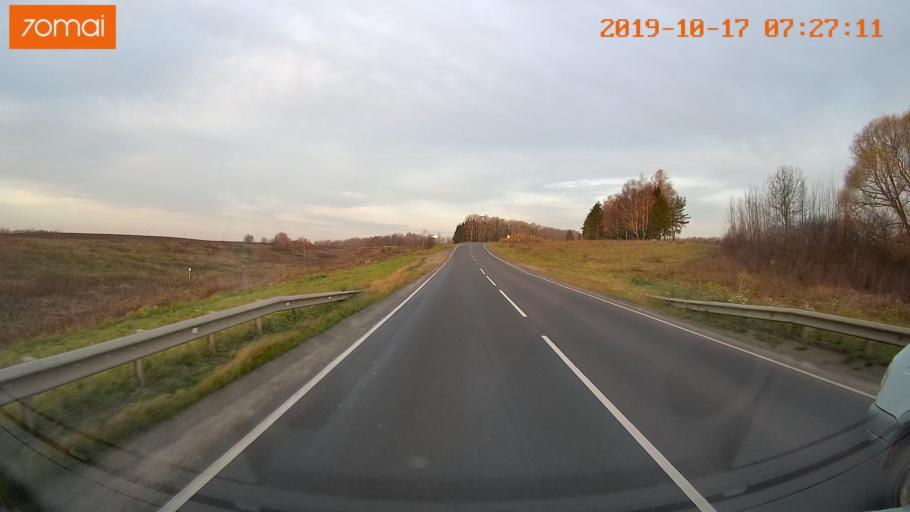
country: RU
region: Ivanovo
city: Gavrilov Posad
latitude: 56.3606
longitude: 40.0819
